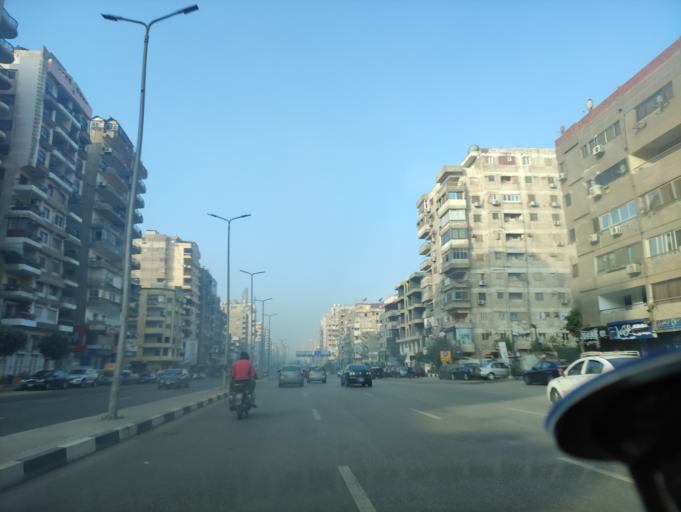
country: EG
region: Muhafazat al Qahirah
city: Cairo
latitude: 30.0551
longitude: 31.3504
